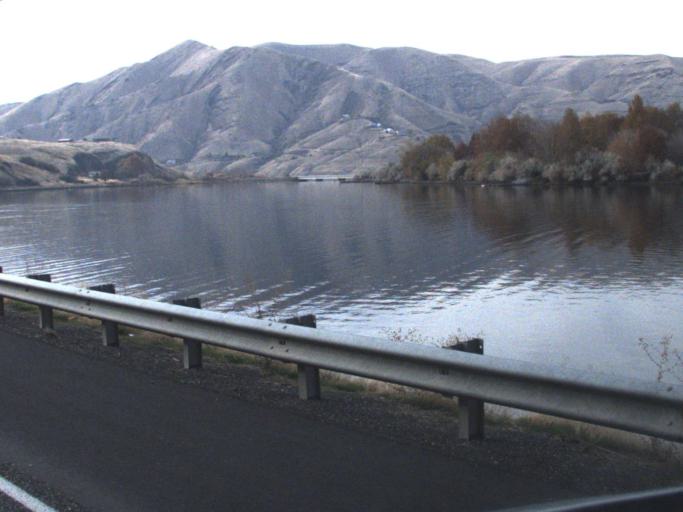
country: US
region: Washington
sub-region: Asotin County
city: Clarkston Heights-Vineland
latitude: 46.4130
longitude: -117.1838
